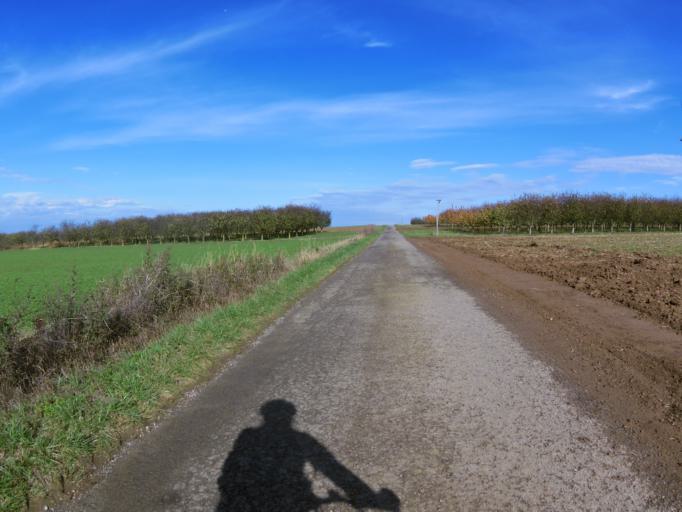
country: DE
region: Bavaria
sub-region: Regierungsbezirk Unterfranken
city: Sommerhausen
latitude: 49.7151
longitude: 10.0388
